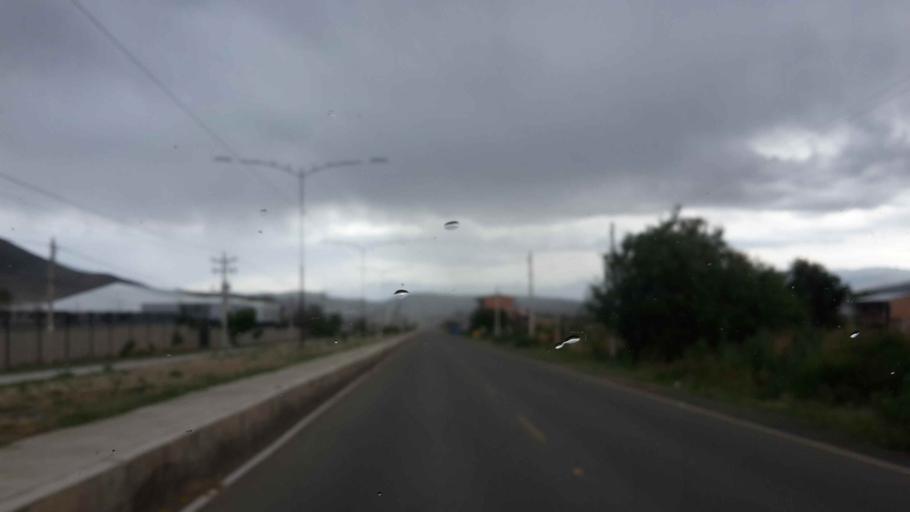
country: BO
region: Cochabamba
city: Tarata
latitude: -17.6005
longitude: -66.0355
